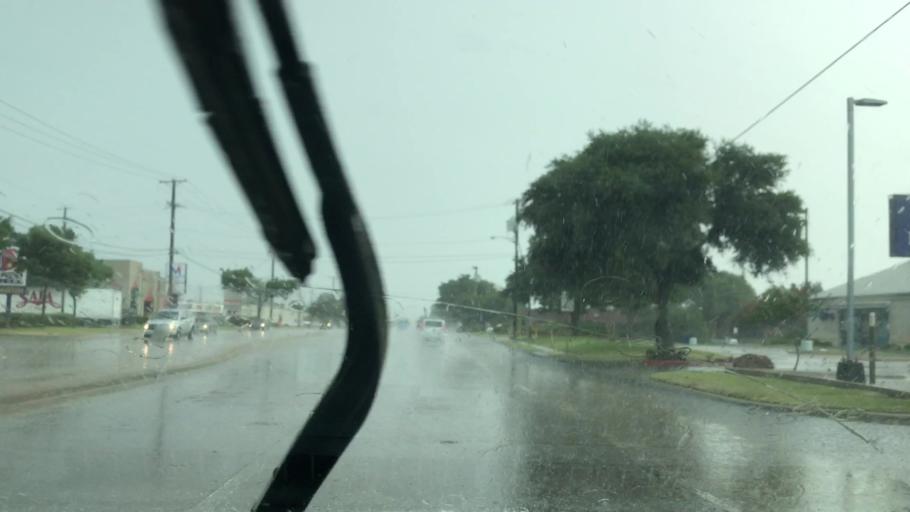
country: US
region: Texas
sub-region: Dallas County
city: Richardson
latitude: 32.9085
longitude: -96.7006
